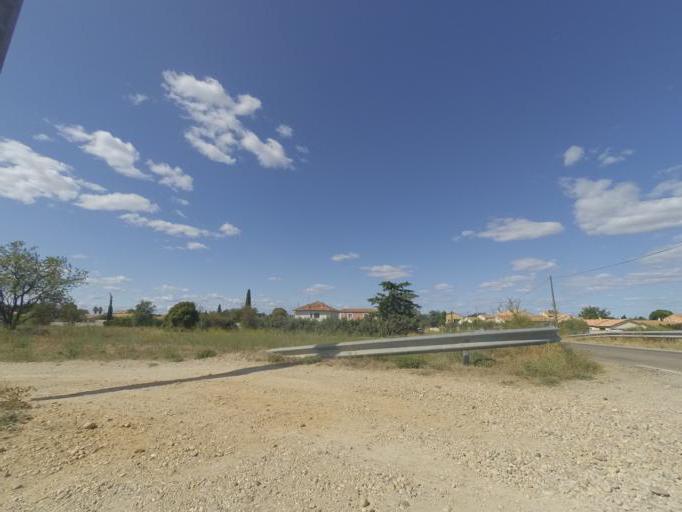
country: FR
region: Languedoc-Roussillon
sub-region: Departement du Gard
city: Codognan
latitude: 43.7245
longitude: 4.2237
